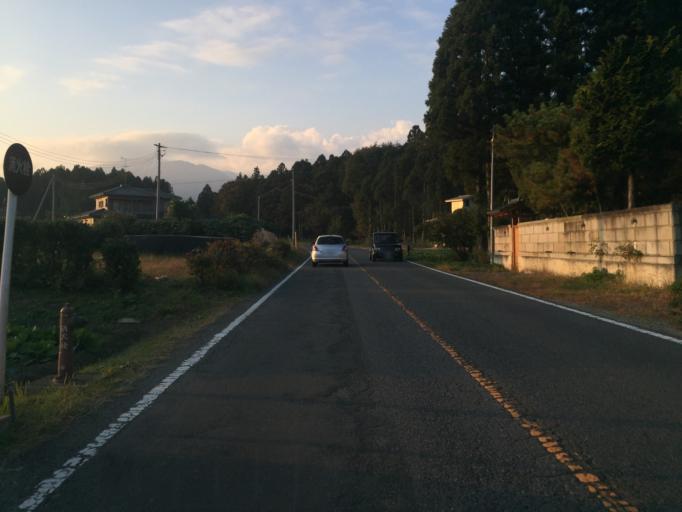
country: JP
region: Fukushima
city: Motomiya
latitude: 37.5521
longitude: 140.3612
